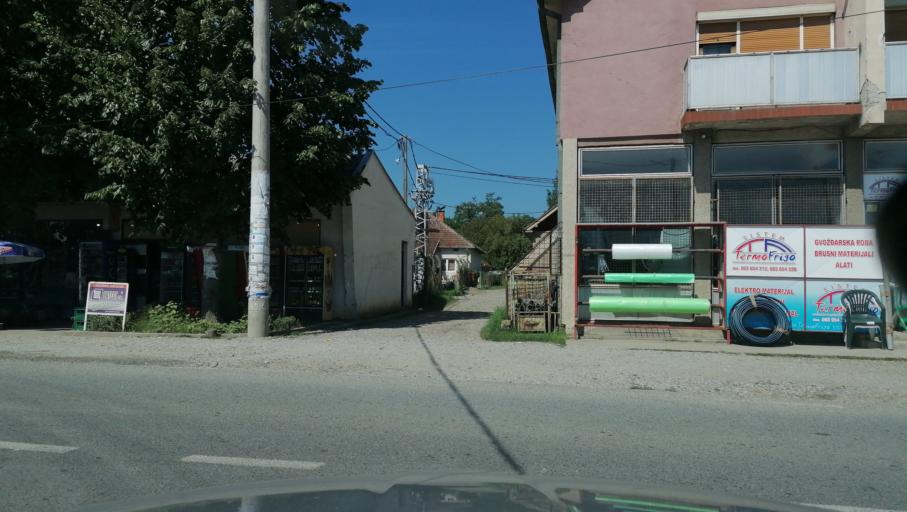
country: RS
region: Central Serbia
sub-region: Raski Okrug
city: Kraljevo
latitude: 43.7253
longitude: 20.7991
